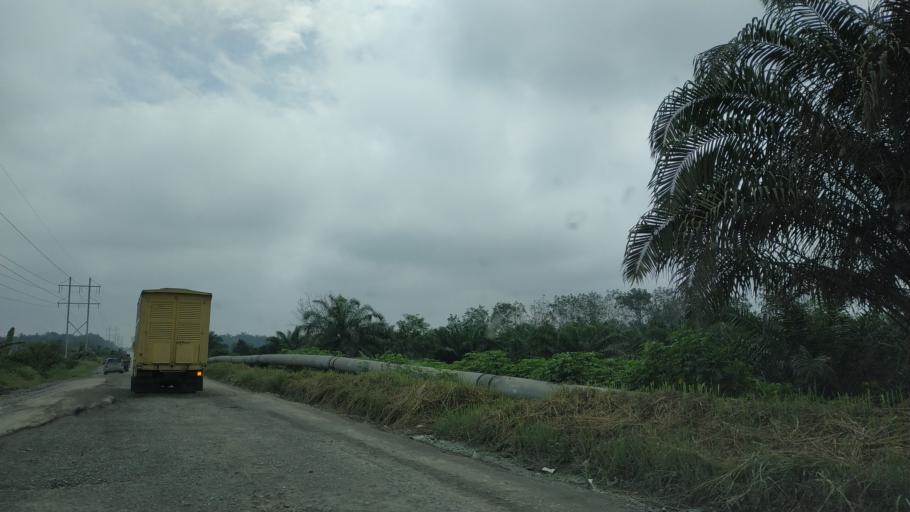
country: ID
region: Riau
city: Siak Sri Indrapura
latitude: 0.6491
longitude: 101.7624
